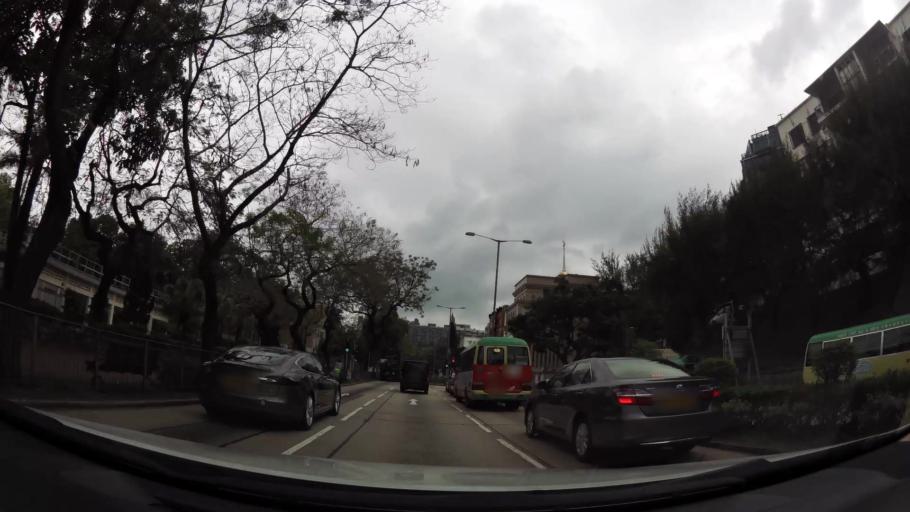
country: HK
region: Wong Tai Sin
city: Wong Tai Sin
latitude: 22.3400
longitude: 114.1785
